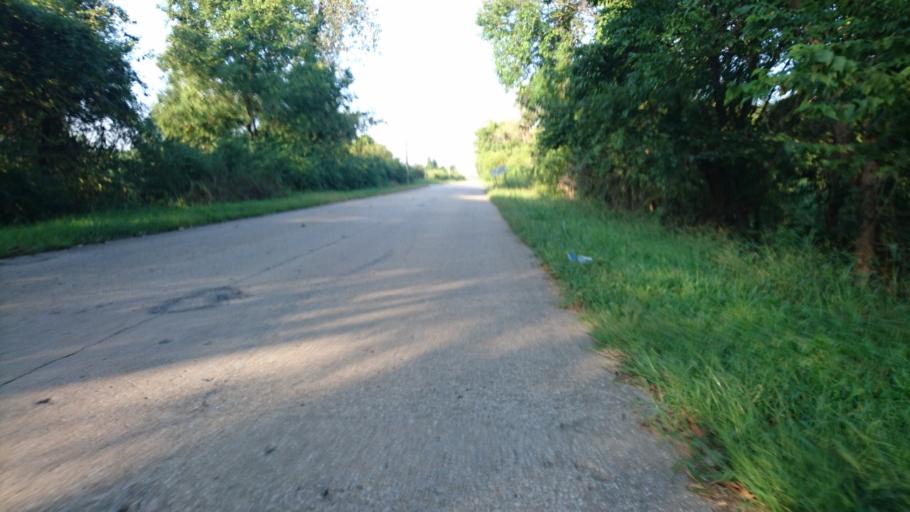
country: US
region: Missouri
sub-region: Saint Louis County
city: Glasgow Village
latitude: 38.7599
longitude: -90.1492
